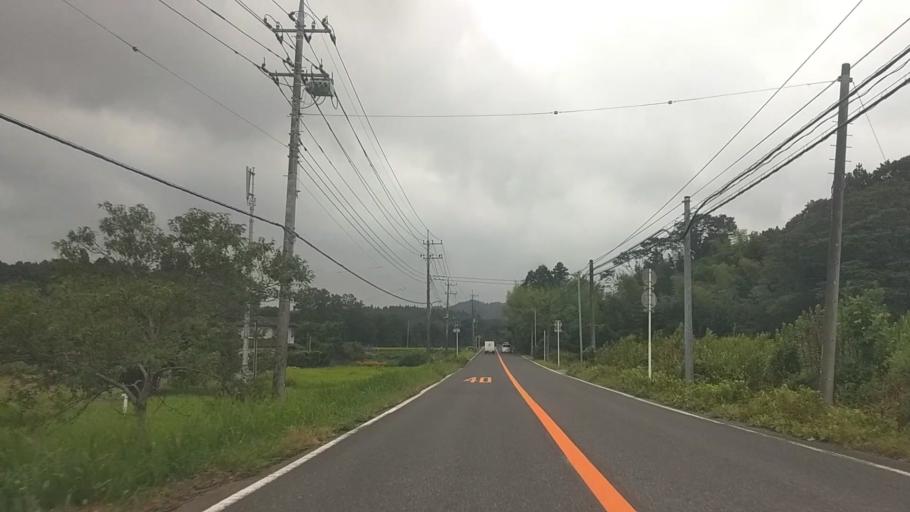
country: JP
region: Chiba
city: Kawaguchi
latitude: 35.2157
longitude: 140.0714
